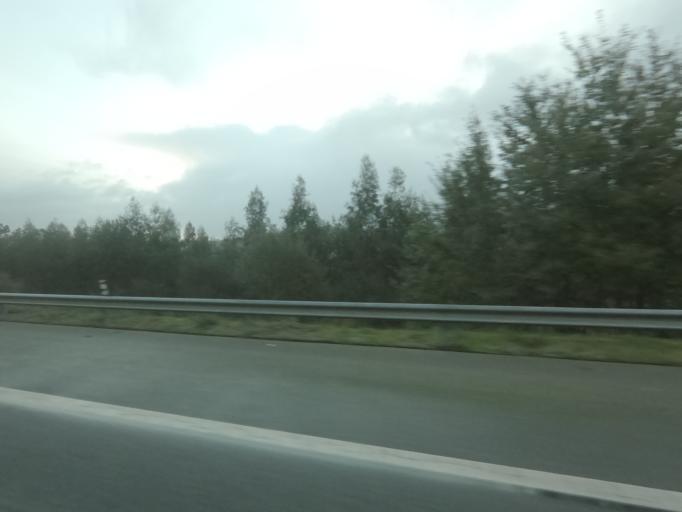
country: PT
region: Braga
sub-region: Barcelos
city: Galegos
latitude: 41.6408
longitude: -8.5578
